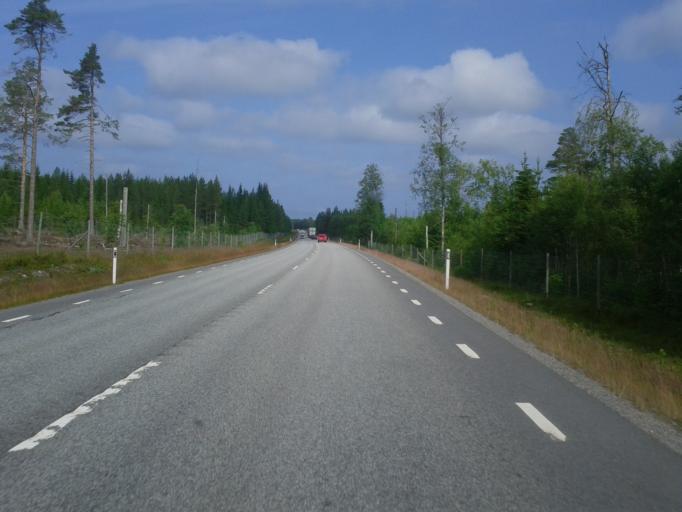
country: SE
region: Vaesterbotten
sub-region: Skelleftea Kommun
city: Burea
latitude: 64.4694
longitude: 21.2928
